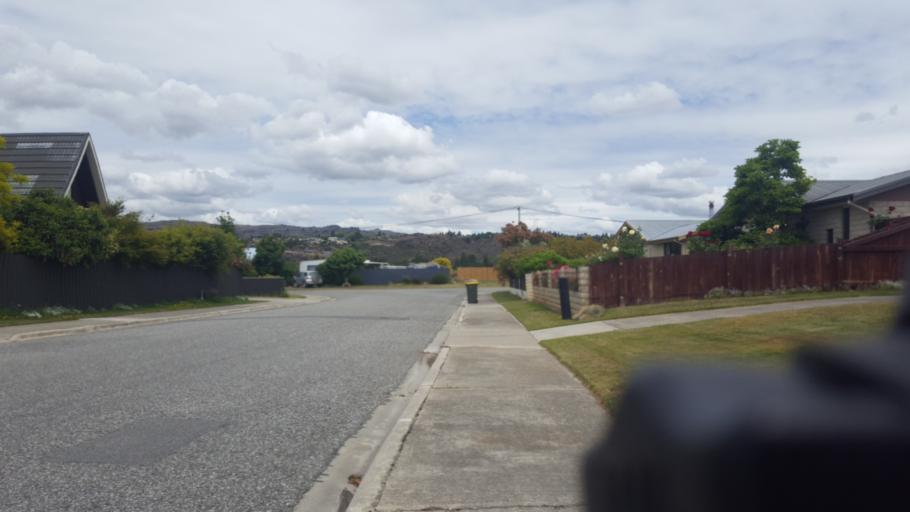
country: NZ
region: Otago
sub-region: Queenstown-Lakes District
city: Wanaka
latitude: -45.2488
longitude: 169.3775
